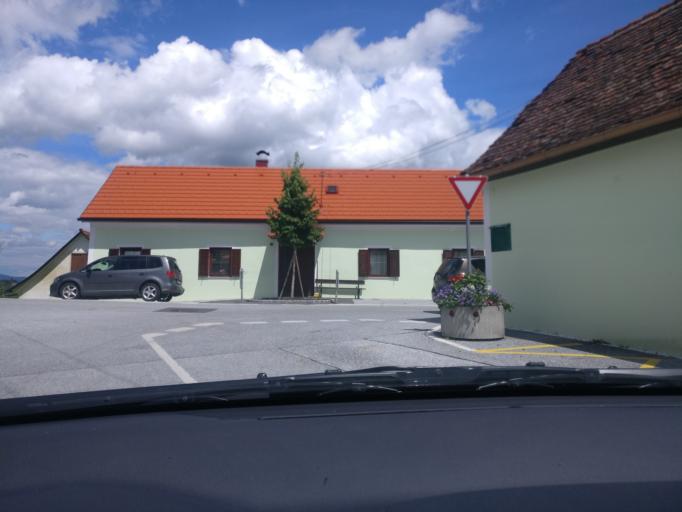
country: AT
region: Styria
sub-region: Politischer Bezirk Weiz
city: Nitscha
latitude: 47.1314
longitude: 15.7296
